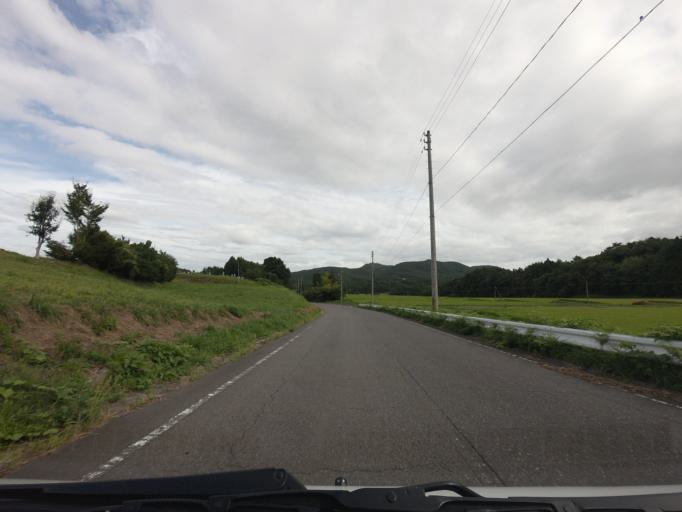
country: JP
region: Fukushima
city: Motomiya
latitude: 37.5414
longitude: 140.3321
